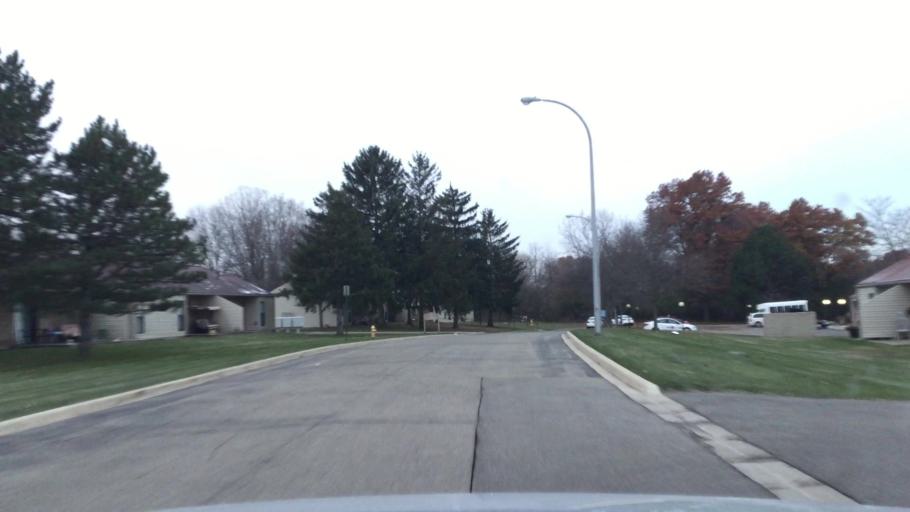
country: US
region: Michigan
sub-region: Oakland County
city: Pontiac
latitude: 42.6276
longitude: -83.2520
